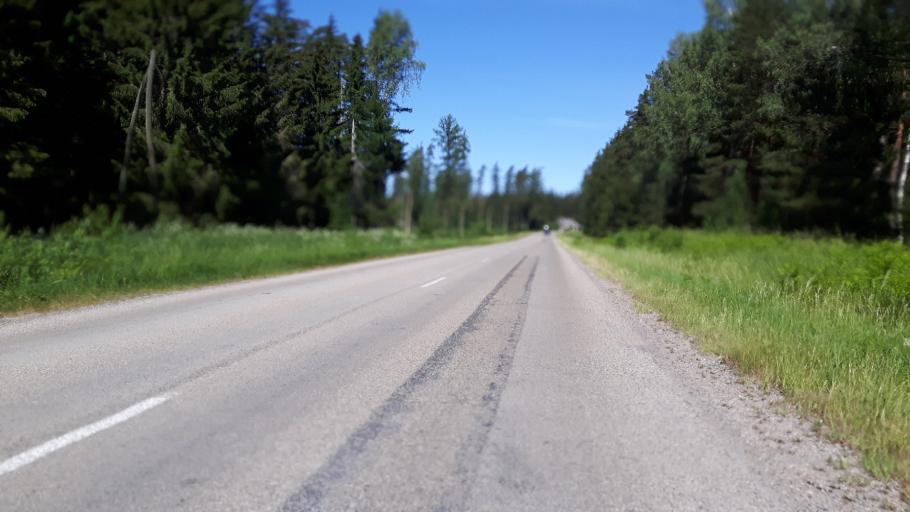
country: LV
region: Tukuma Rajons
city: Tukums
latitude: 57.0094
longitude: 23.0559
